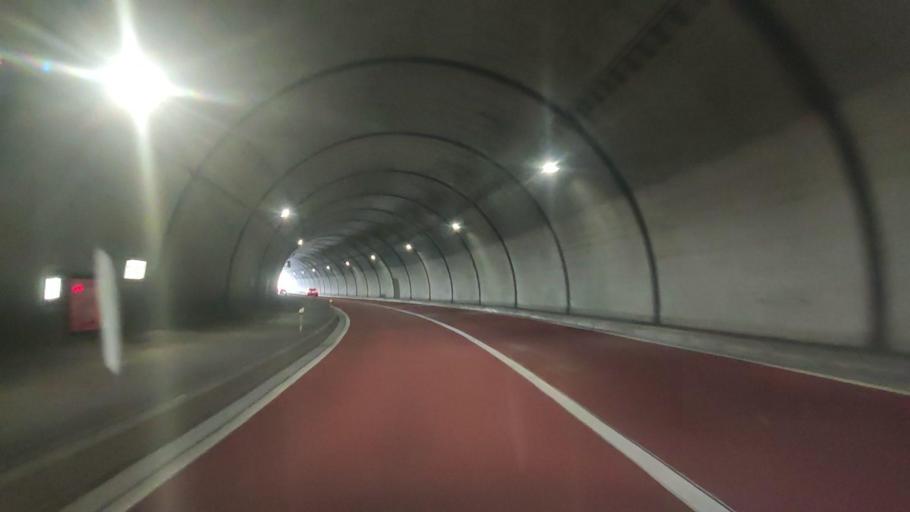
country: JP
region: Oita
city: Oita
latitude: 33.0928
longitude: 131.6498
